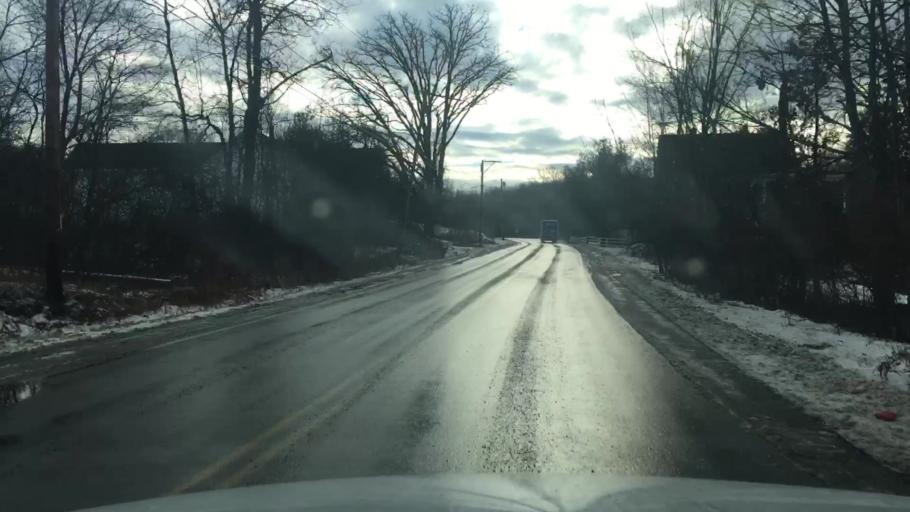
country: US
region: Maine
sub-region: Penobscot County
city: Brewer
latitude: 44.7632
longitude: -68.7760
